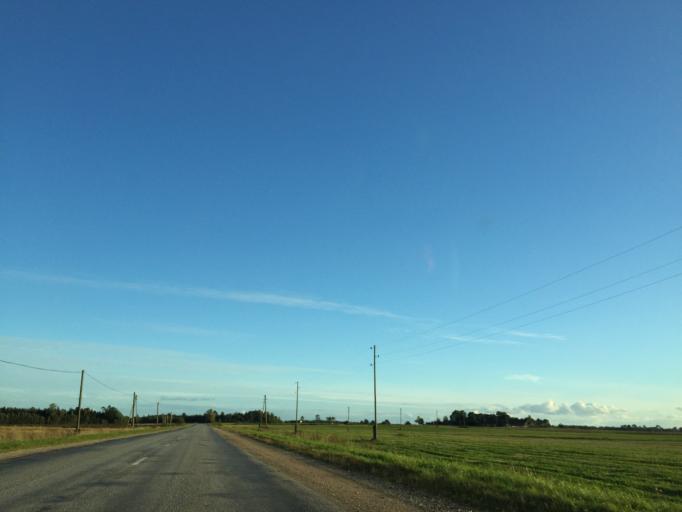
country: LV
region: Saldus Rajons
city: Saldus
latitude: 56.7405
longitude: 22.3774
